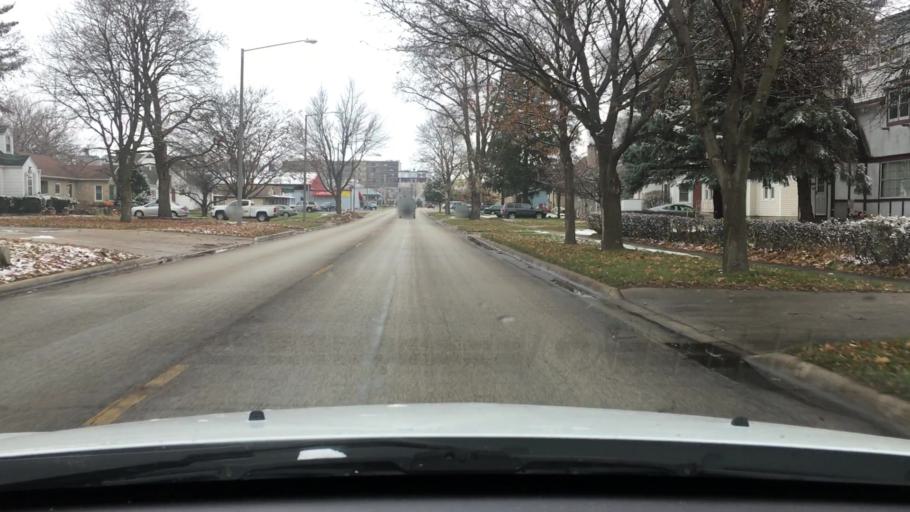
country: US
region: Illinois
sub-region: Ogle County
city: Rochelle
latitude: 41.9313
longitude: -89.0665
